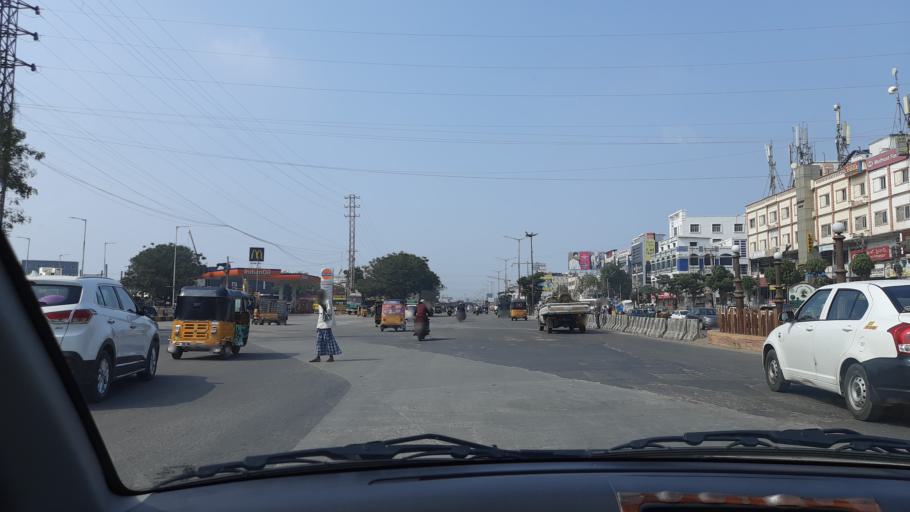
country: IN
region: Telangana
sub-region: Rangareddi
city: Lal Bahadur Nagar
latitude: 17.3421
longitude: 78.5573
